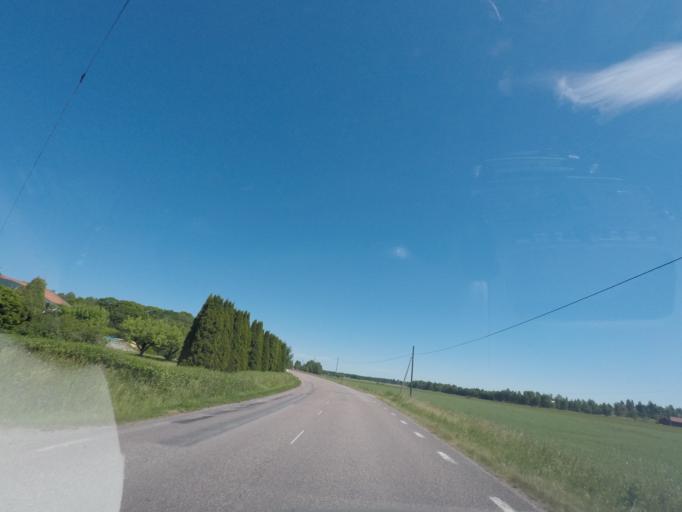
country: SE
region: Vaestmanland
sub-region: Vasteras
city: Tillberga
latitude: 59.6358
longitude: 16.6693
